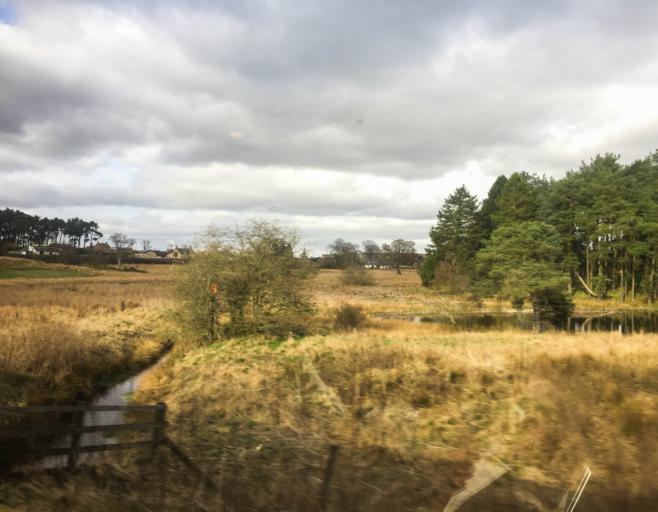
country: GB
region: Scotland
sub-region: South Lanarkshire
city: Carluke
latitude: 55.7195
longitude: -3.8371
